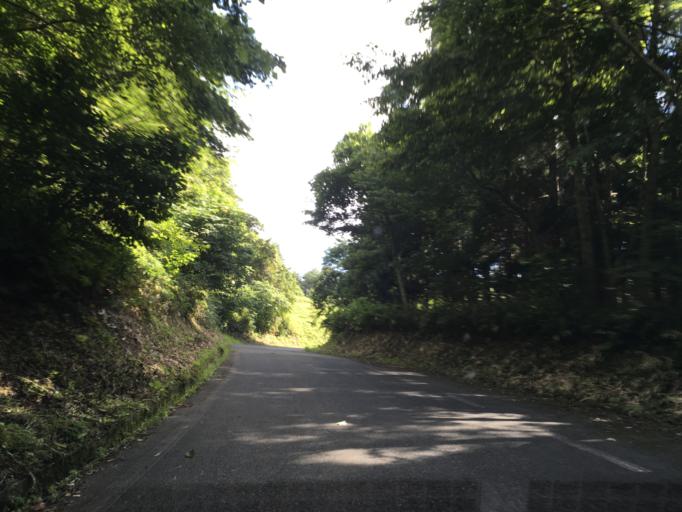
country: JP
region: Iwate
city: Ofunato
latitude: 38.9769
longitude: 141.4373
